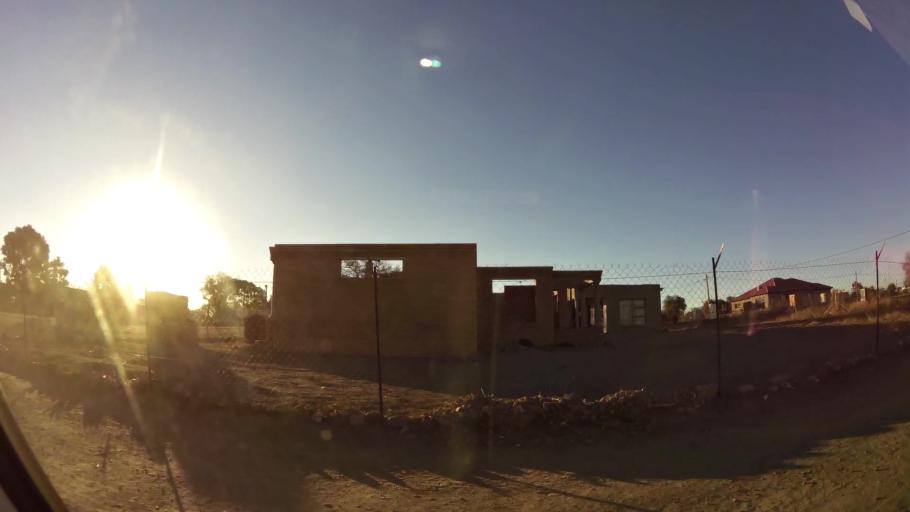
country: ZA
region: Limpopo
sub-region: Capricorn District Municipality
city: Polokwane
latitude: -23.8247
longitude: 29.3770
